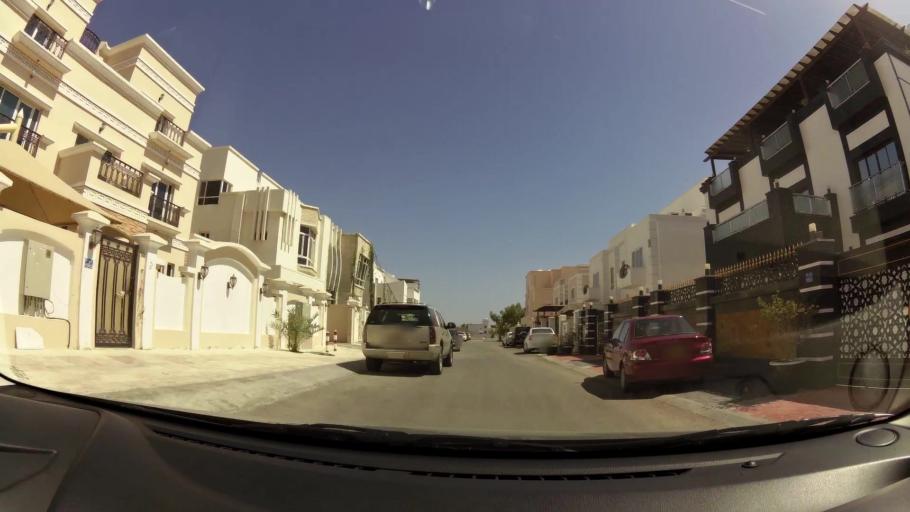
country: OM
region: Muhafazat Masqat
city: As Sib al Jadidah
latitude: 23.5964
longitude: 58.2430
